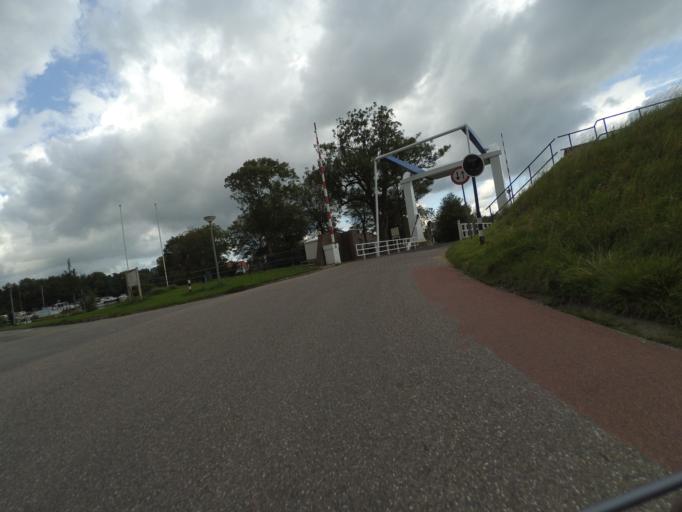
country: NL
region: North Holland
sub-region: Gemeente Schagen
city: Schagen
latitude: 52.8833
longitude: 4.8755
